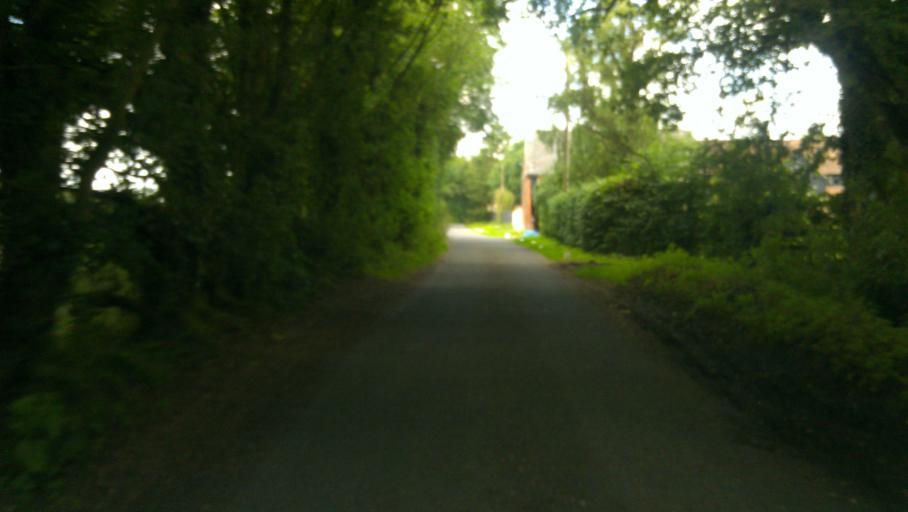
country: GB
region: England
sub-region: Essex
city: Rayne
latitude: 51.8617
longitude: 0.6345
